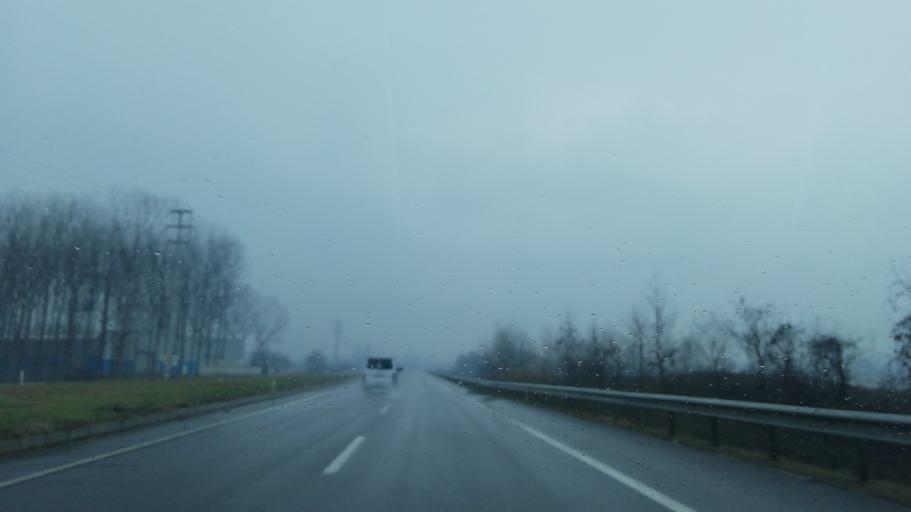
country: TR
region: Sakarya
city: Akyazi
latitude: 40.6484
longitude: 30.6060
